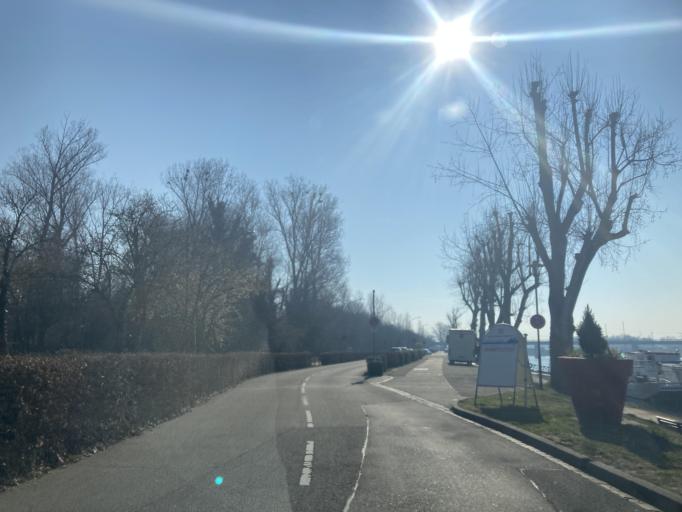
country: DE
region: Baden-Wuerttemberg
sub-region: Freiburg Region
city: Breisach am Rhein
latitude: 48.0266
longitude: 7.5786
